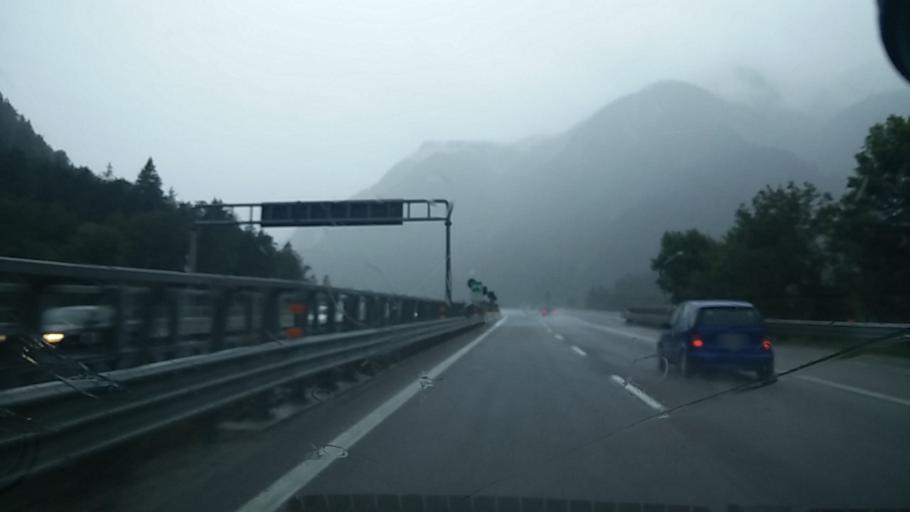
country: IT
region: Friuli Venezia Giulia
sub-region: Provincia di Udine
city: Malborghetto
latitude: 46.5076
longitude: 13.4712
